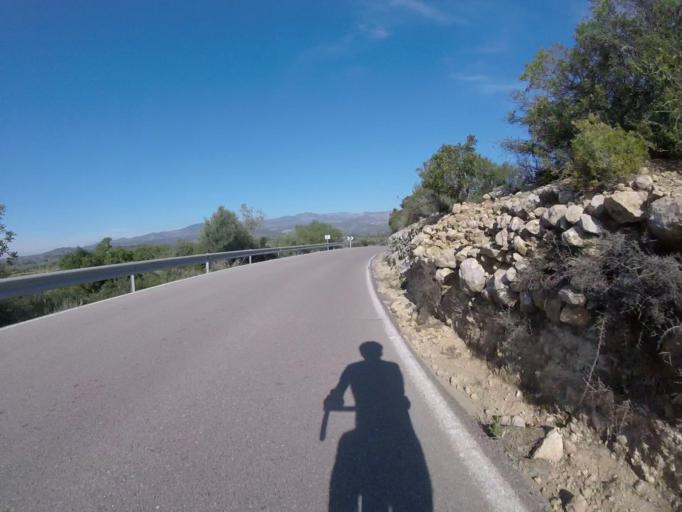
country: ES
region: Valencia
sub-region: Provincia de Castello
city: Benlloch
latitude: 40.2462
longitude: 0.0772
